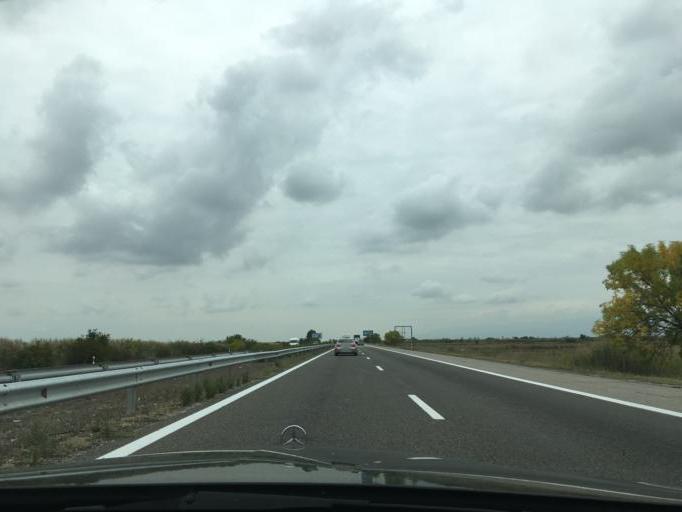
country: BG
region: Pazardzhik
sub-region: Obshtina Pazardzhik
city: Pazardzhik
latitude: 42.2547
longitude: 24.3334
